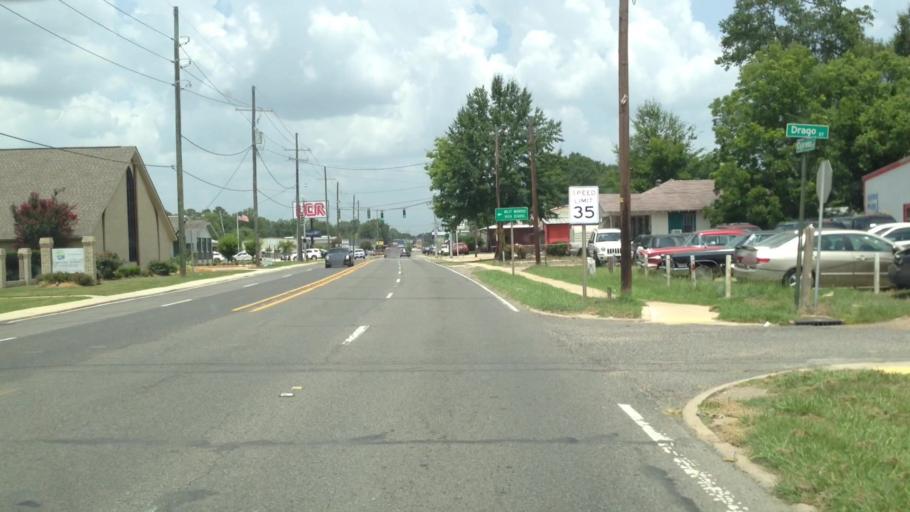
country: US
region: Louisiana
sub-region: Ouachita Parish
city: West Monroe
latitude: 32.5112
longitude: -92.1345
